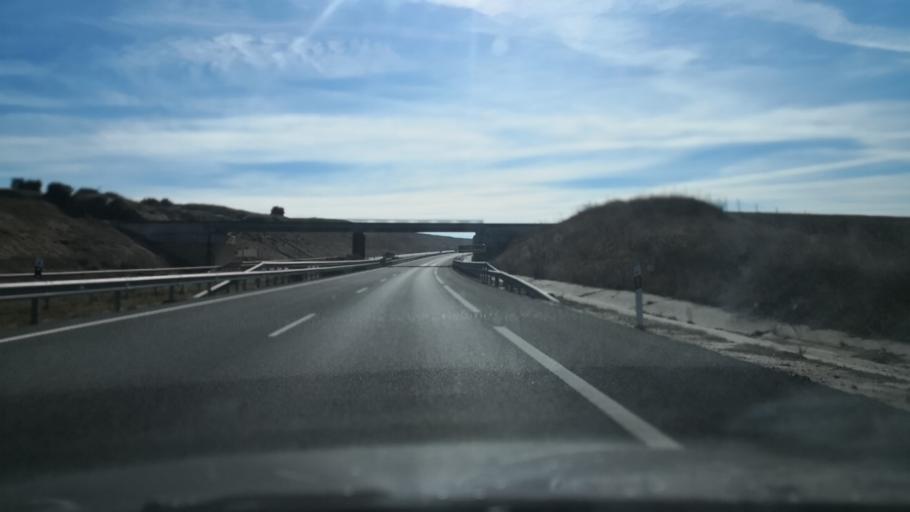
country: ES
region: Castille and Leon
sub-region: Provincia de Avila
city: Crespos
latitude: 40.8711
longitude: -4.9882
